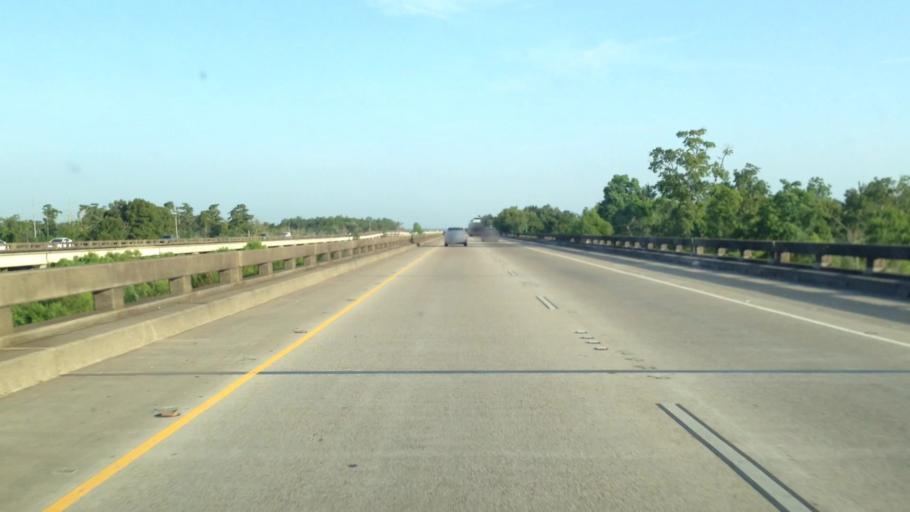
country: US
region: Louisiana
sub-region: Saint Charles Parish
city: Norco
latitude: 30.0520
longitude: -90.3661
